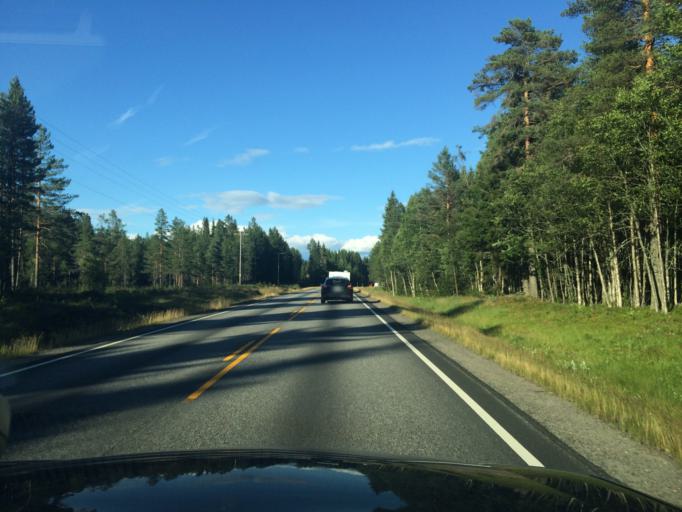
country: NO
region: Hedmark
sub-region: Elverum
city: Elverum
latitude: 61.0154
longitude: 11.8425
